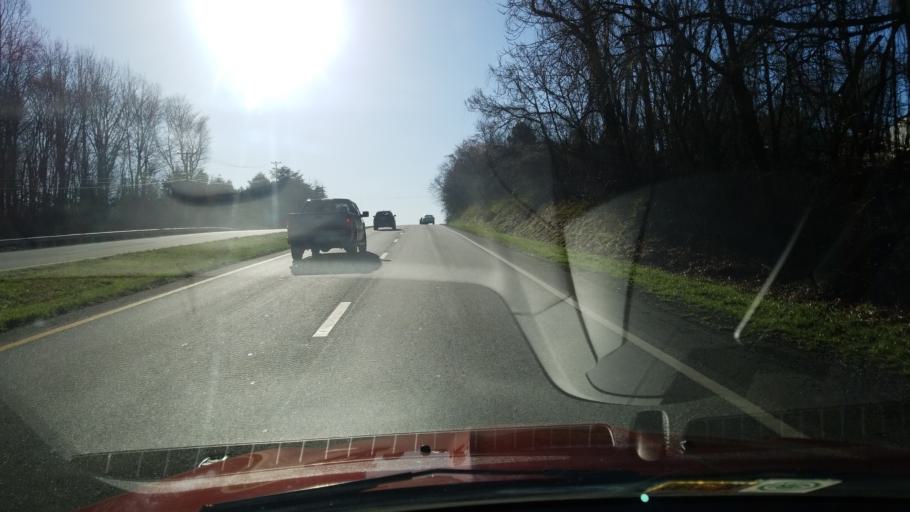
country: US
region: Virginia
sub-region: Franklin County
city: Rocky Mount
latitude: 37.0862
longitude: -79.9303
